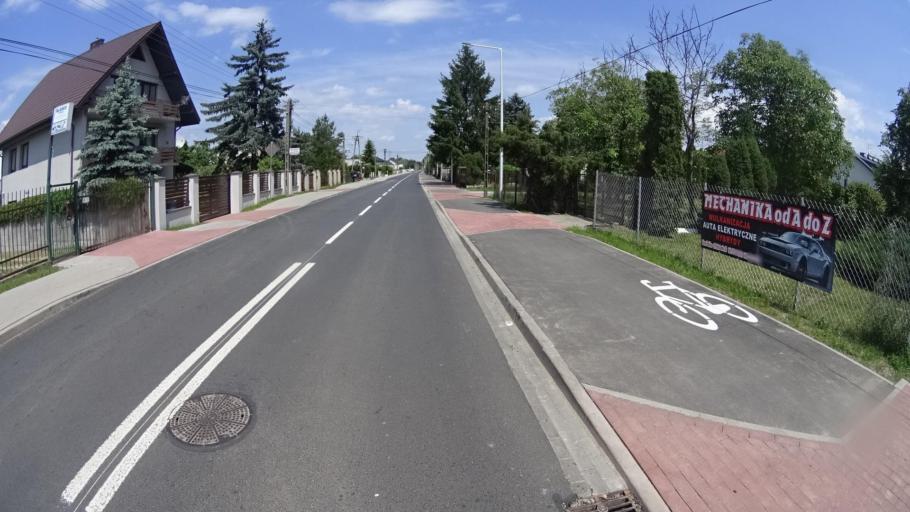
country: PL
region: Masovian Voivodeship
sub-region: Powiat warszawski zachodni
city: Stare Babice
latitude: 52.2586
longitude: 20.8392
